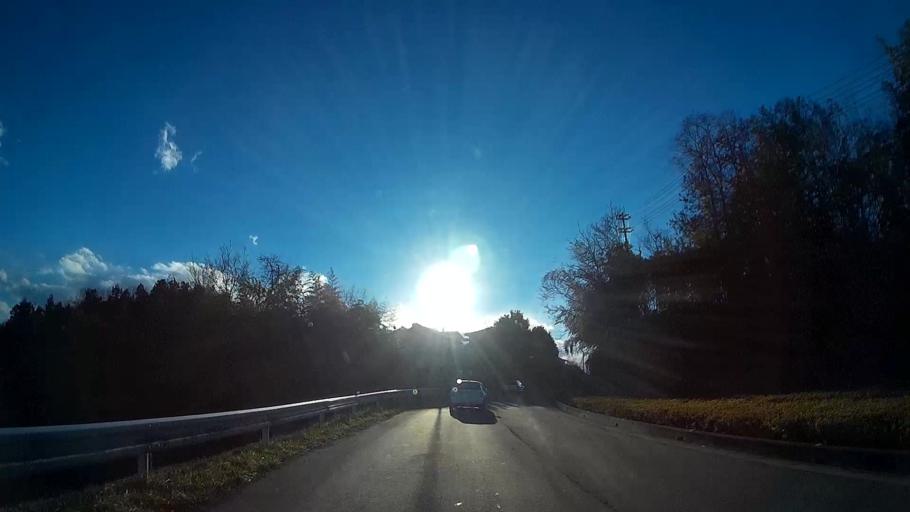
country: JP
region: Saitama
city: Chichibu
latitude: 36.0585
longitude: 139.0786
